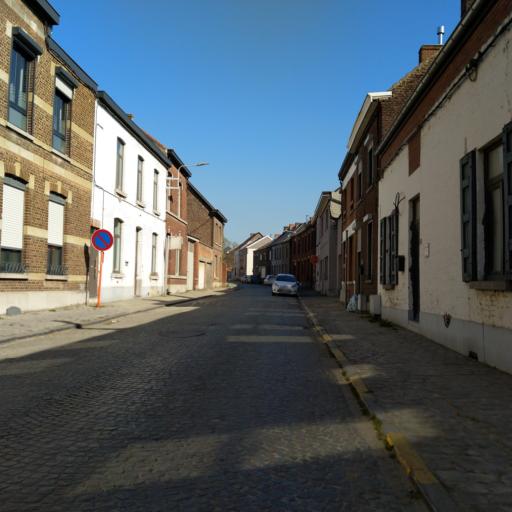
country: BE
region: Wallonia
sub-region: Province du Hainaut
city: Mons
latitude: 50.4697
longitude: 3.9594
